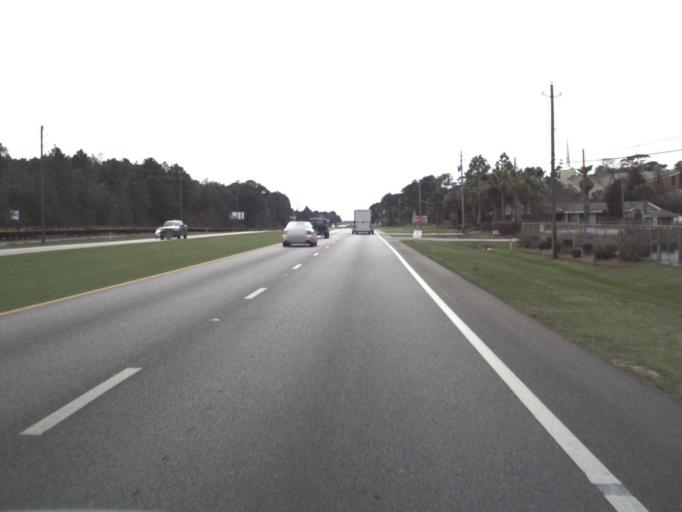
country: US
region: Florida
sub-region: Bay County
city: Hiland Park
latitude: 30.2096
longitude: -85.6127
